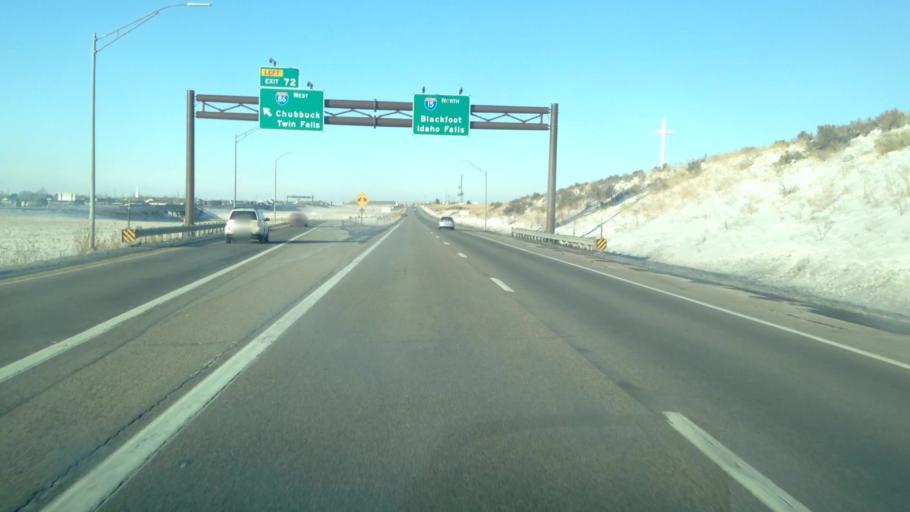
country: US
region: Idaho
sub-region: Bannock County
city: Chubbuck
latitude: 42.9056
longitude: -112.4397
